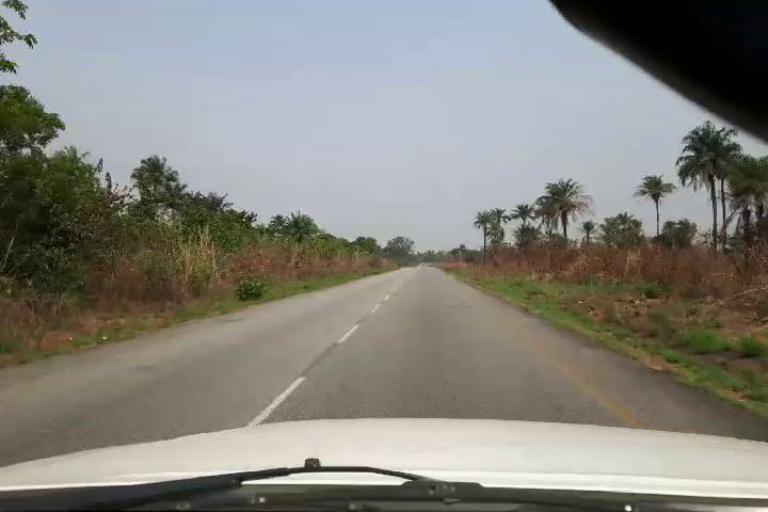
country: SL
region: Southern Province
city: Largo
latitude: 8.3078
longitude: -12.2080
